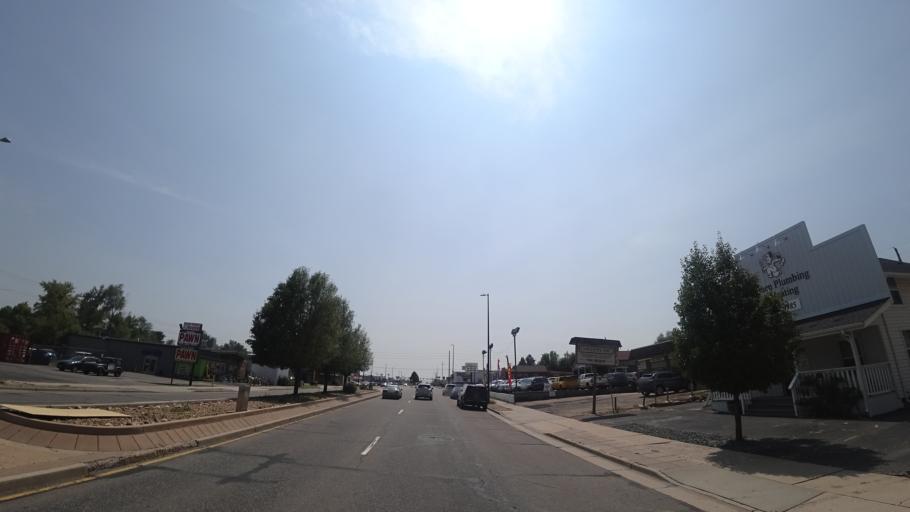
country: US
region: Colorado
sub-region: Arapahoe County
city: Englewood
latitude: 39.6307
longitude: -104.9880
